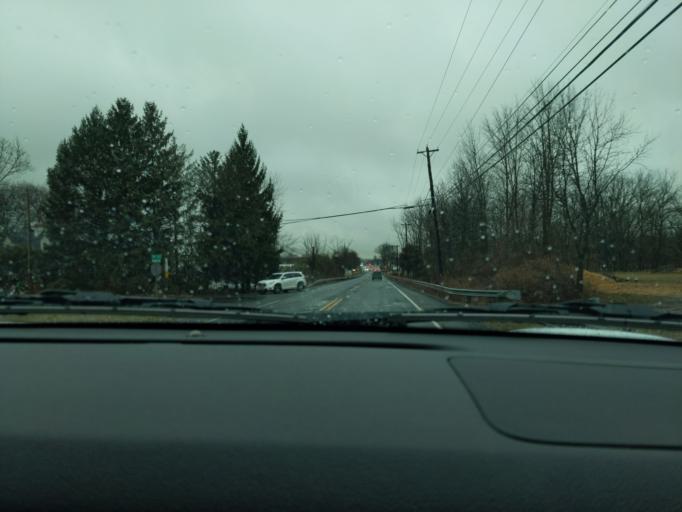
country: US
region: Pennsylvania
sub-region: Bucks County
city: Dublin
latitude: 40.3792
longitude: -75.2146
